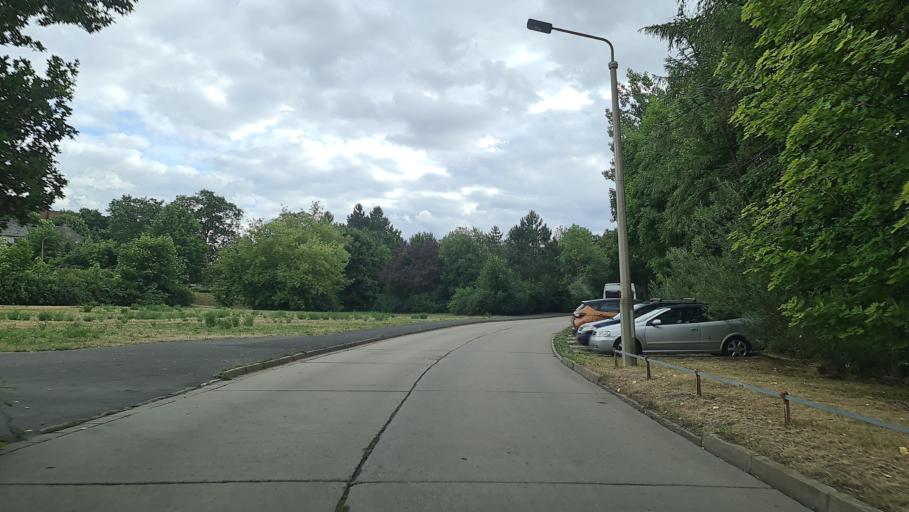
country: DE
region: Saxony
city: Plauen
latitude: 50.4985
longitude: 12.1596
